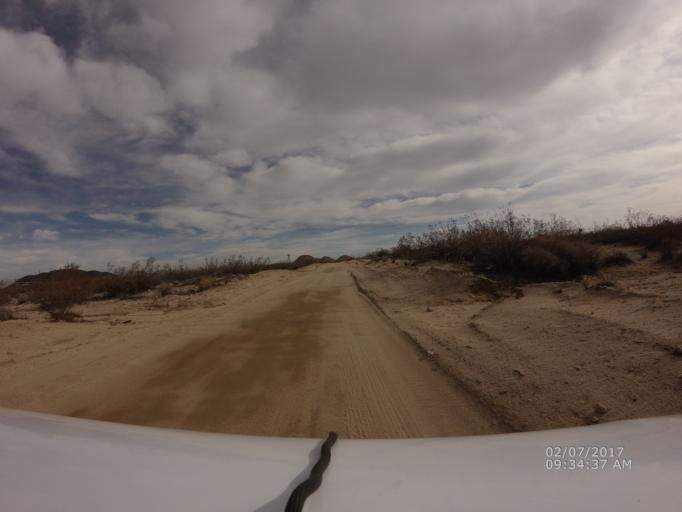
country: US
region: California
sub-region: San Bernardino County
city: Pinon Hills
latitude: 34.5246
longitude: -117.7283
